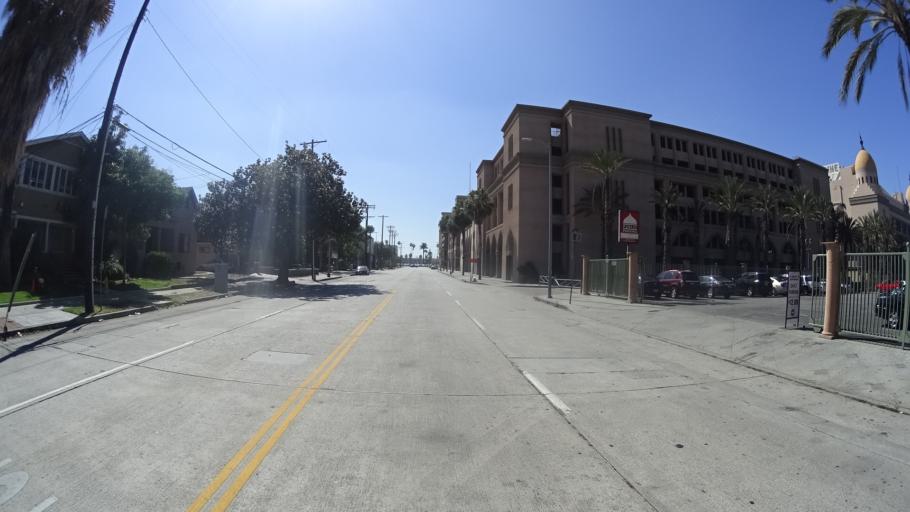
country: US
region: California
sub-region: Los Angeles County
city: Los Angeles
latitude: 34.0249
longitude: -118.2817
